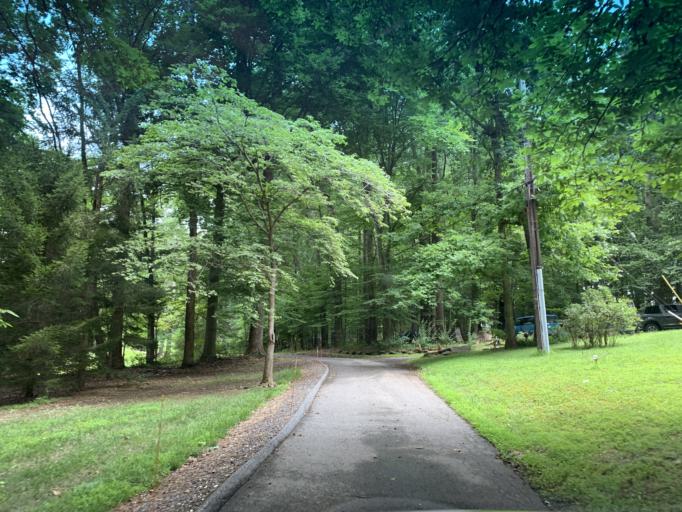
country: US
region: Maryland
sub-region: Baltimore County
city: Kingsville
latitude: 39.4455
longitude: -76.4514
